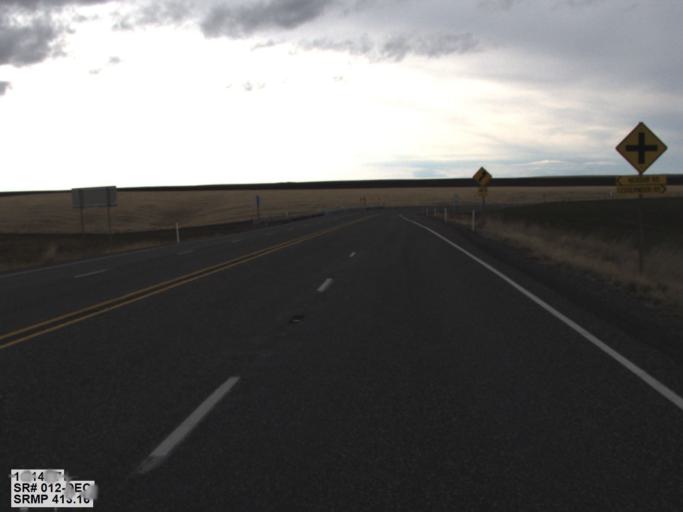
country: US
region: Washington
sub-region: Garfield County
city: Pomeroy
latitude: 46.4359
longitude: -117.4284
